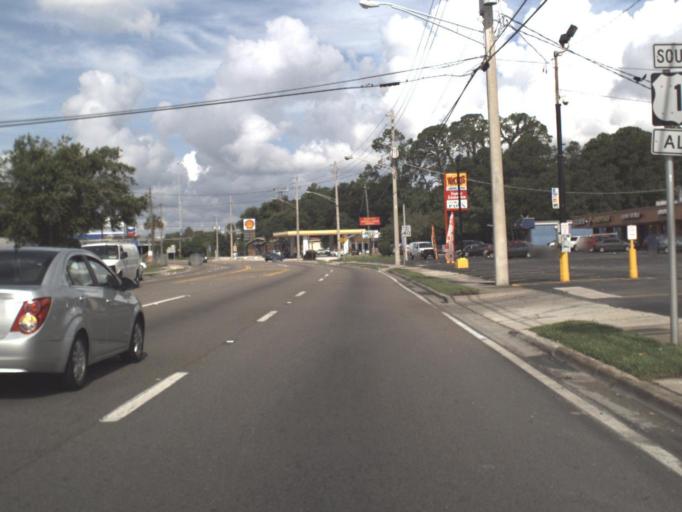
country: US
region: Florida
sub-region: Duval County
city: Jacksonville
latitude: 30.2912
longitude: -81.6263
